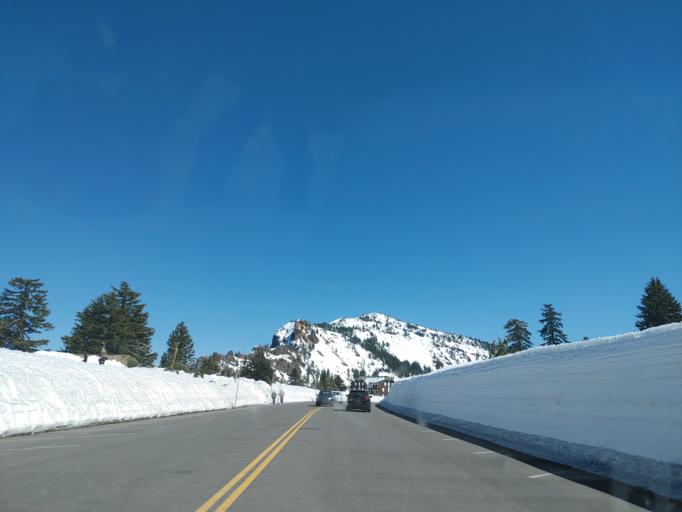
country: US
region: Oregon
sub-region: Jackson County
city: Shady Cove
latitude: 42.9111
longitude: -122.1446
